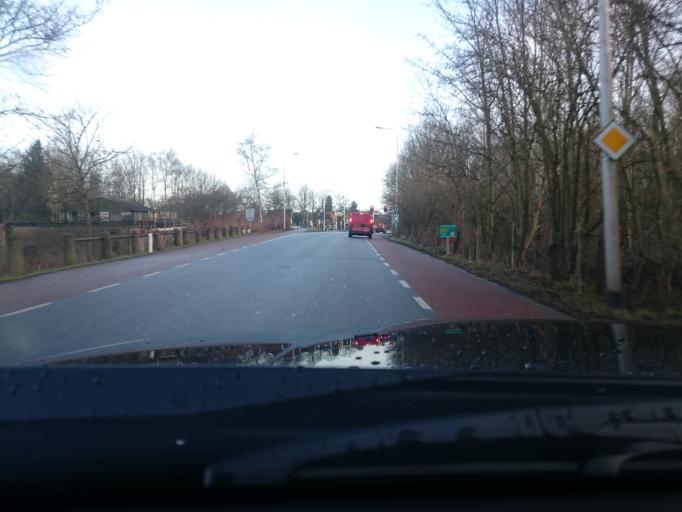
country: NL
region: Overijssel
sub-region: Gemeente Deventer
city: Deventer
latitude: 52.2449
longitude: 6.1431
